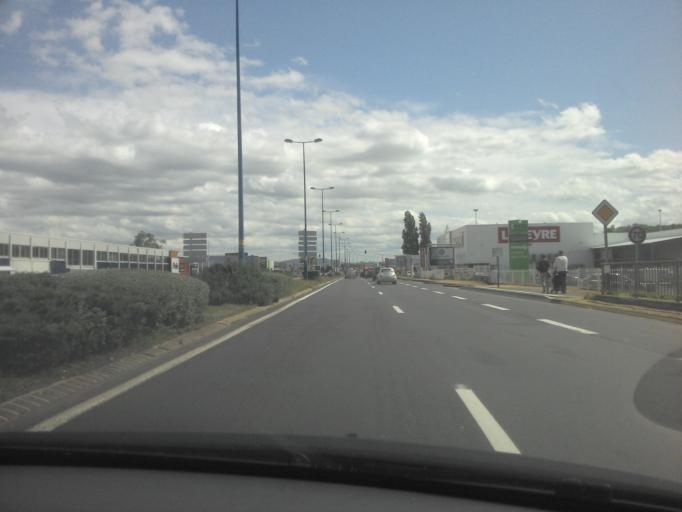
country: FR
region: Auvergne
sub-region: Departement du Puy-de-Dome
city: Aubiere
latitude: 45.7569
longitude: 3.1278
